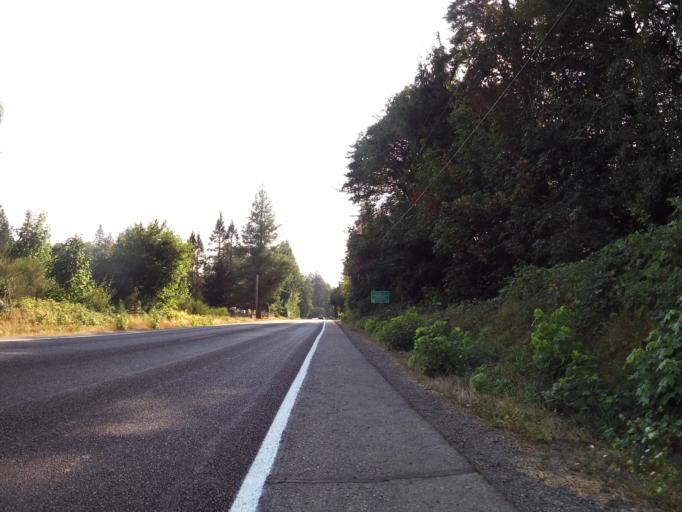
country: US
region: Washington
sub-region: Mason County
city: Belfair
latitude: 47.5136
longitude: -122.7848
